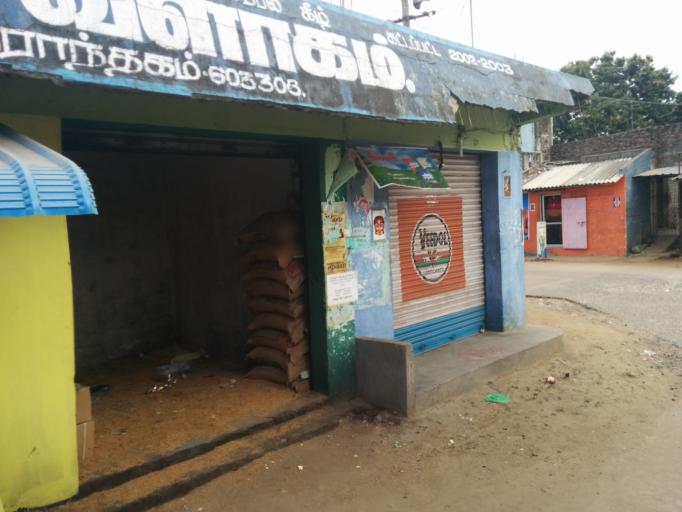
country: IN
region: Tamil Nadu
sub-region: Kancheepuram
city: Madurantakam
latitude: 12.5117
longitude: 79.8848
